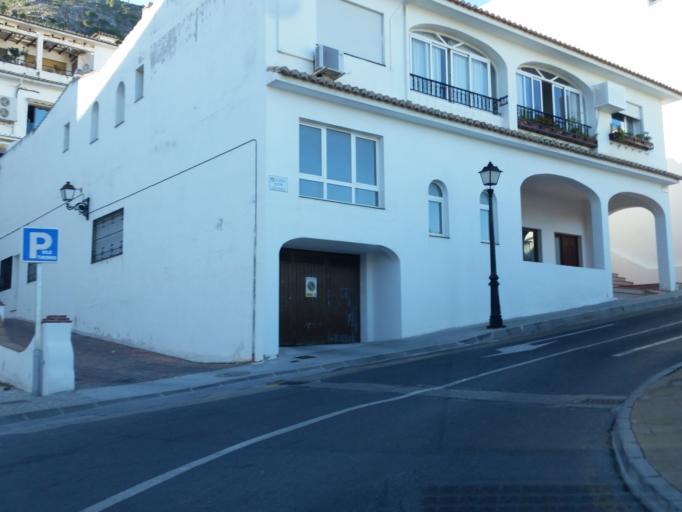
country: ES
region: Andalusia
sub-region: Provincia de Malaga
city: Mijas
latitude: 36.5969
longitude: -4.6363
